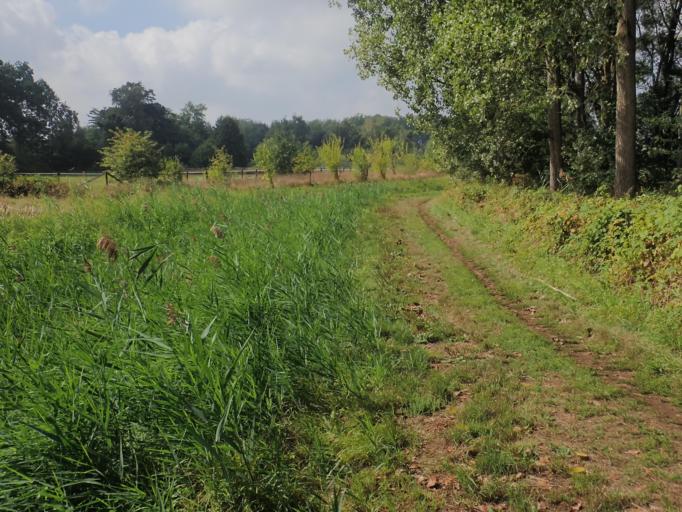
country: BE
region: Flanders
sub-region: Provincie Vlaams-Brabant
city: Keerbergen
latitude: 51.0140
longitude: 4.6612
